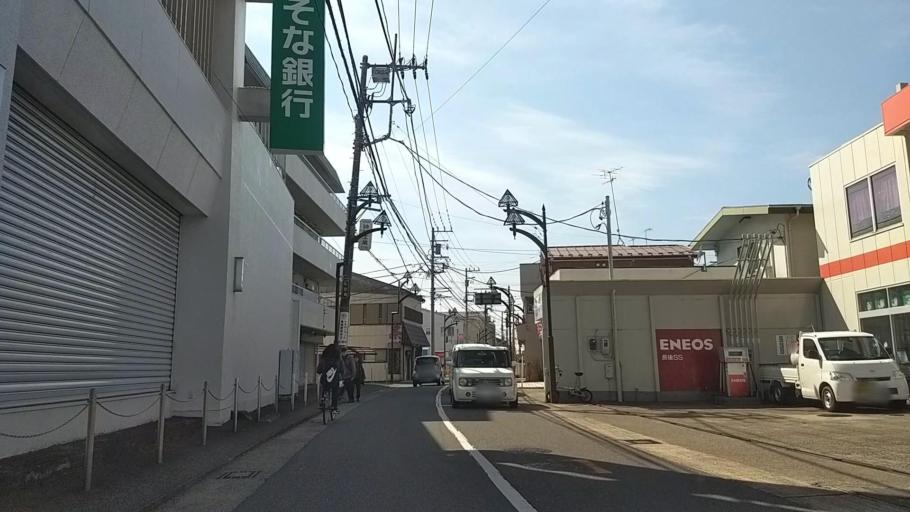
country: JP
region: Kanagawa
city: Fujisawa
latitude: 35.4132
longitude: 139.4645
